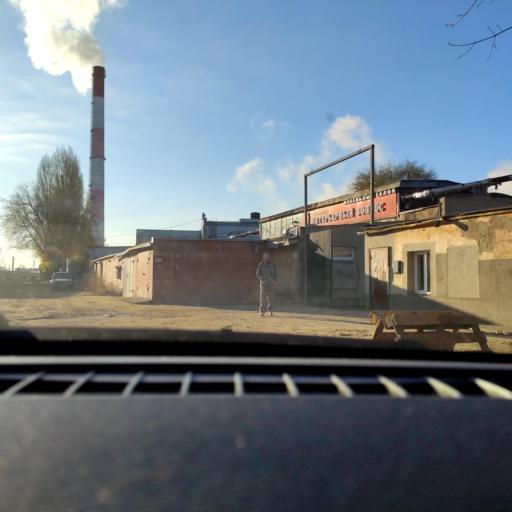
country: RU
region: Voronezj
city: Voronezh
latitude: 51.6344
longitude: 39.2504
